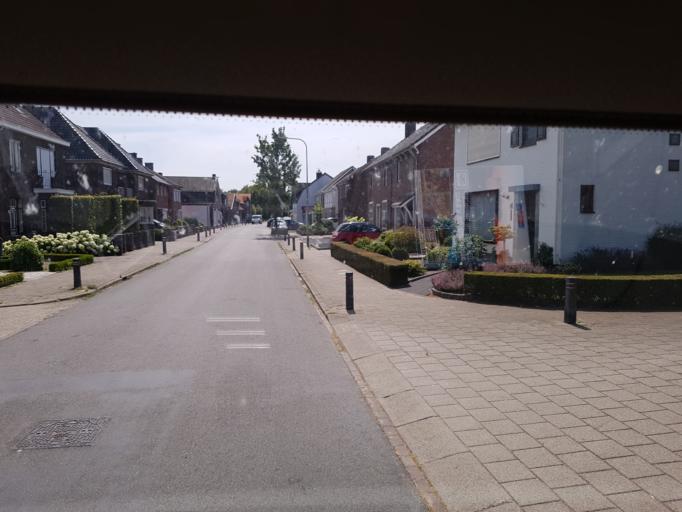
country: NL
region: Limburg
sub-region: Gemeente Leudal
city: Kelpen-Oler
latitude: 51.1920
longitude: 5.8115
